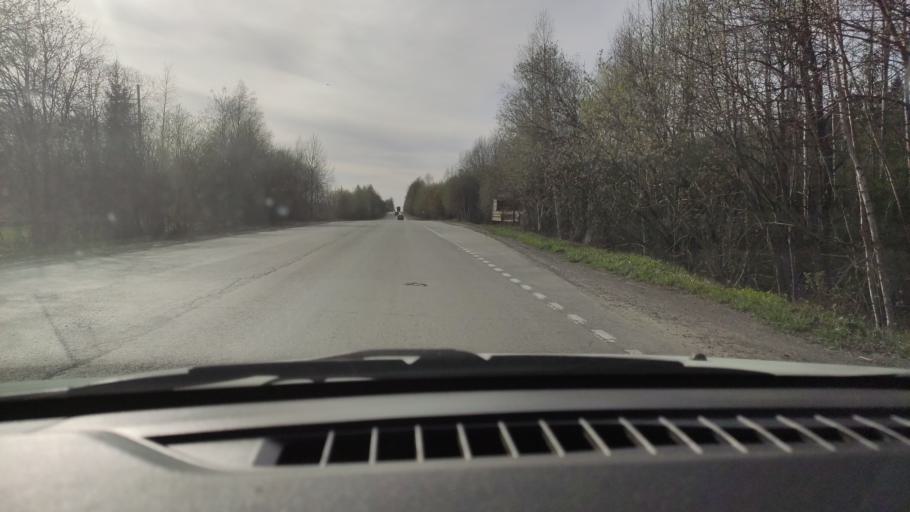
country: RU
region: Perm
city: Ferma
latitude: 57.9399
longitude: 56.4479
